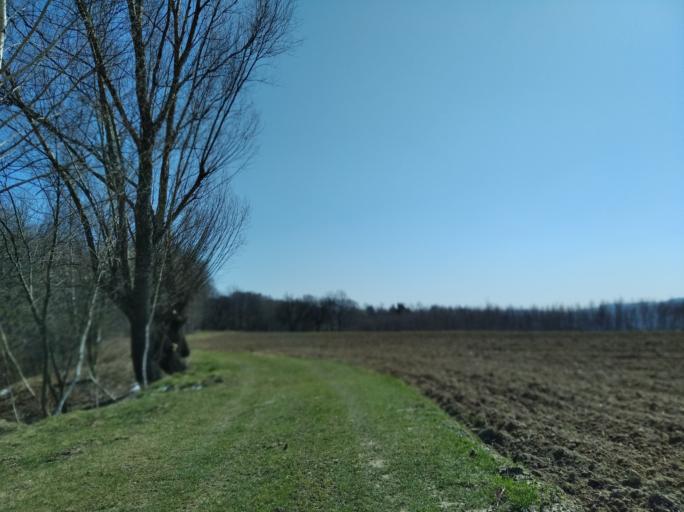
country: PL
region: Subcarpathian Voivodeship
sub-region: Powiat strzyzowski
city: Strzyzow
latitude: 49.8528
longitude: 21.8164
